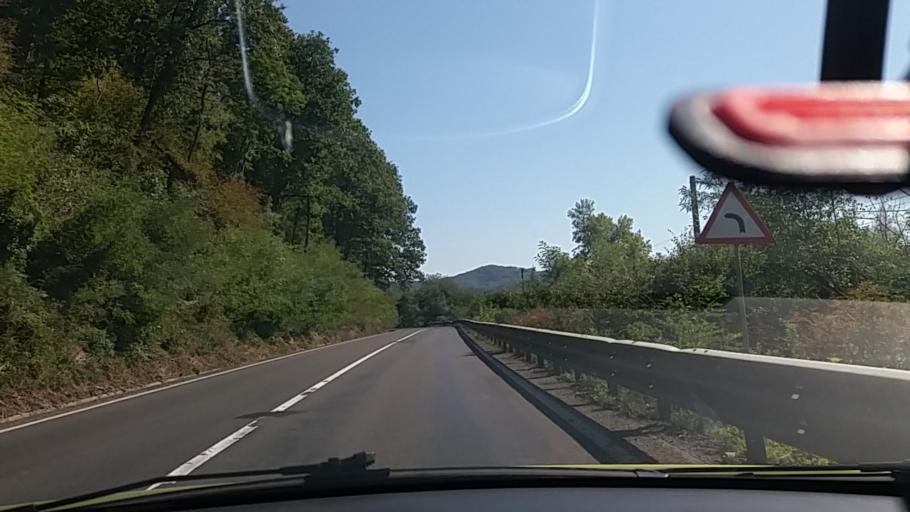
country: RO
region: Hunedoara
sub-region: Comuna Zam
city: Zam
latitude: 46.0129
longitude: 22.4287
